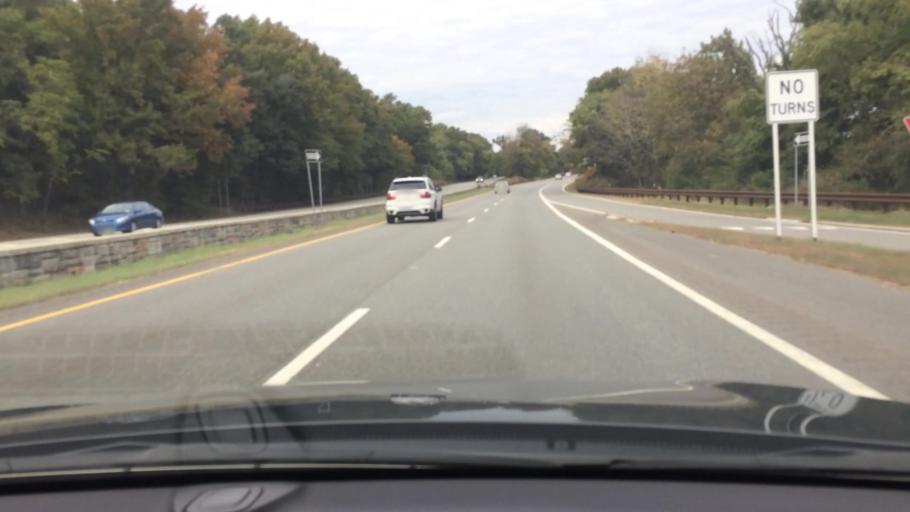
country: US
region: New Jersey
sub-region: Bergen County
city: Englewood Cliffs
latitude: 40.8814
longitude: -73.9477
